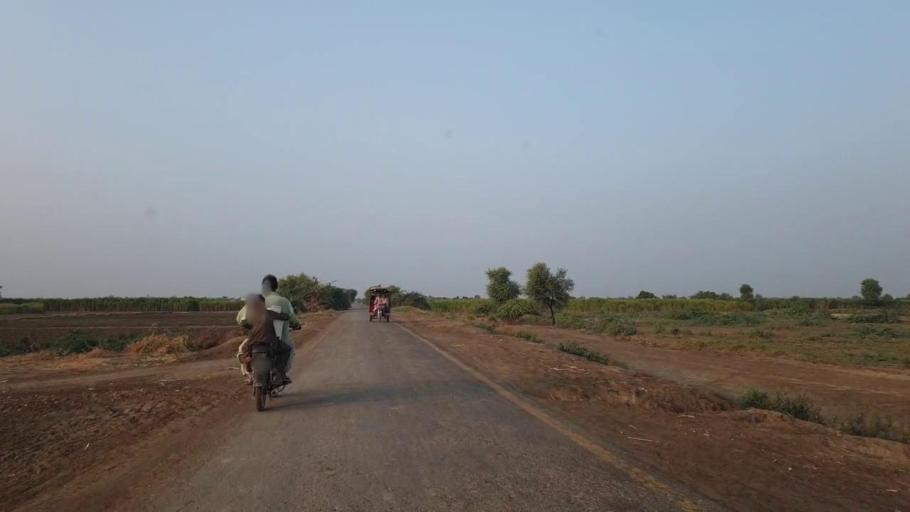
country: PK
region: Sindh
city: Tando Ghulam Ali
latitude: 25.1334
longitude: 68.9587
